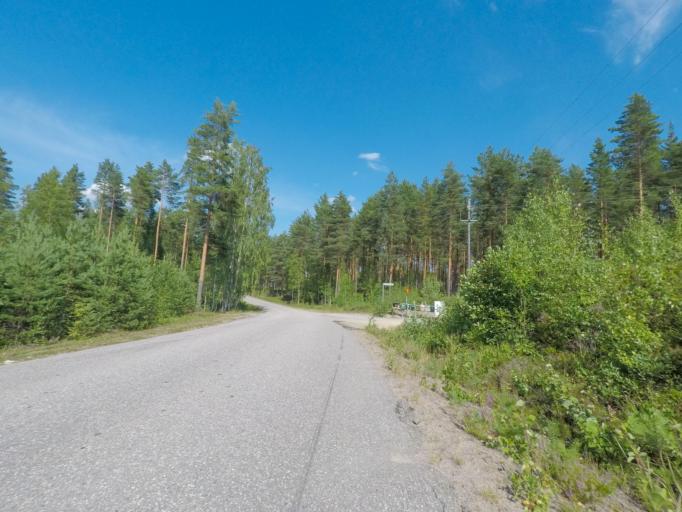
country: FI
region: Southern Savonia
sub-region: Mikkeli
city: Puumala
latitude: 61.4304
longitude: 28.1695
